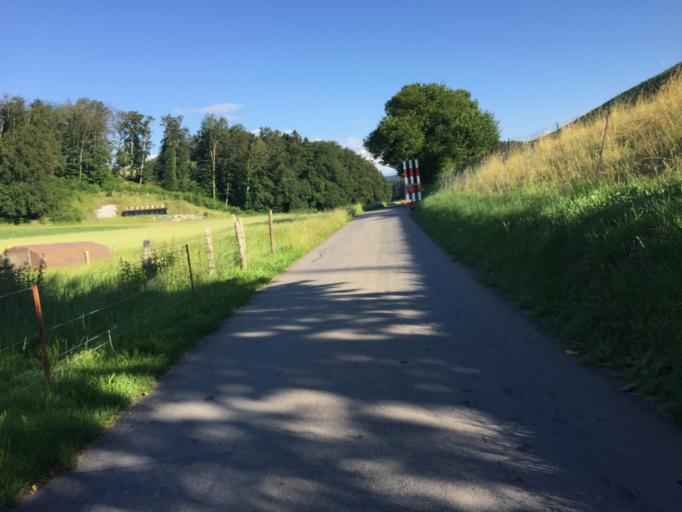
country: CH
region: Bern
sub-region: Bern-Mittelland District
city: Niederwichtrach
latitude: 46.8413
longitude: 7.5813
